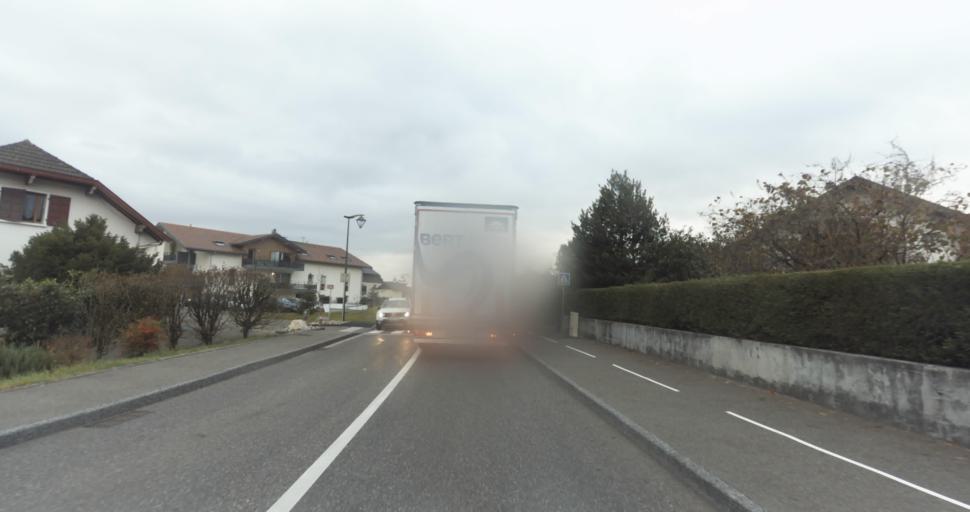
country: FR
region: Rhone-Alpes
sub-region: Departement de la Haute-Savoie
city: Pringy
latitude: 45.9405
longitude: 6.1381
